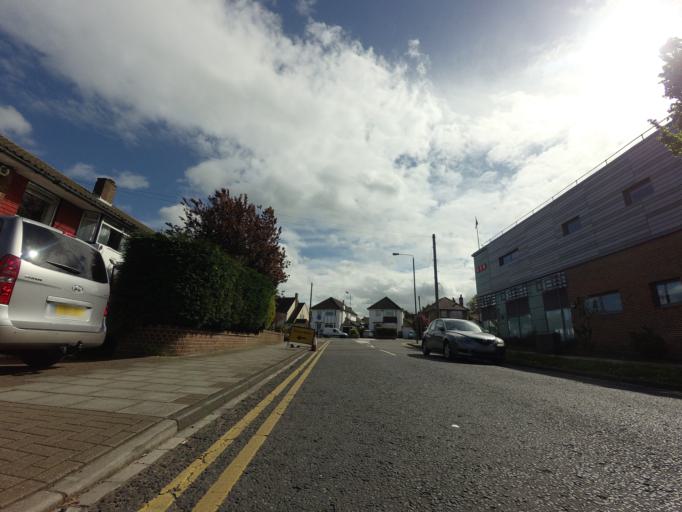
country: GB
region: England
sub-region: Greater London
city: Orpington
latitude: 51.3724
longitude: 0.1111
